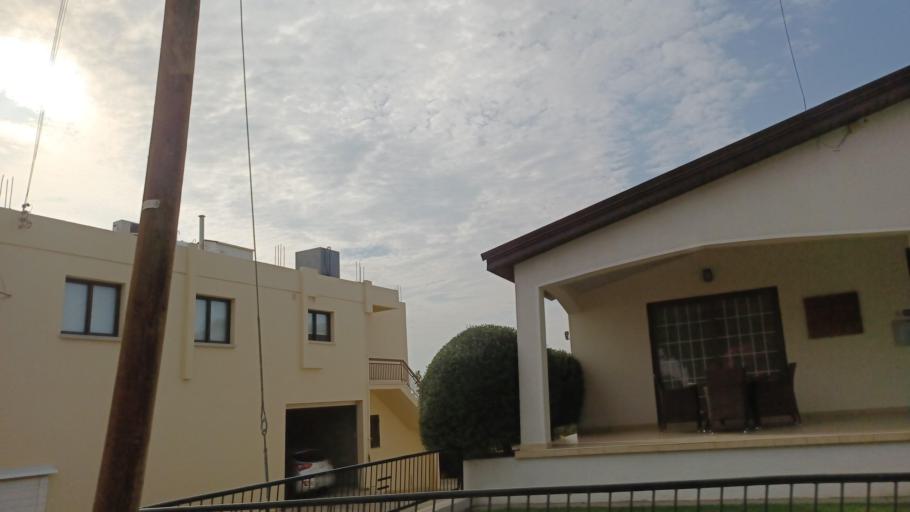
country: CY
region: Lefkosia
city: Peristerona
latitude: 35.1073
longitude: 33.0947
